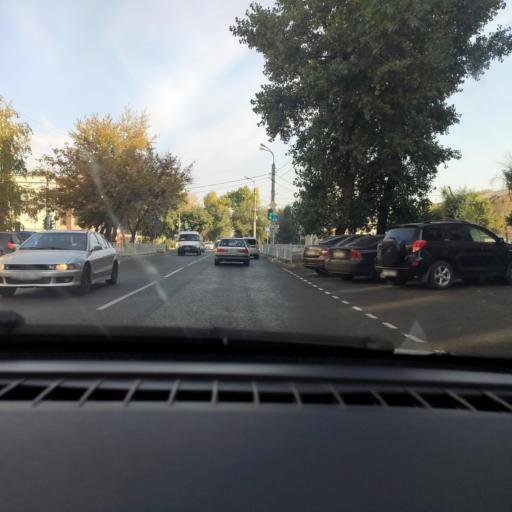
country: RU
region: Voronezj
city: Voronezh
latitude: 51.6381
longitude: 39.2389
